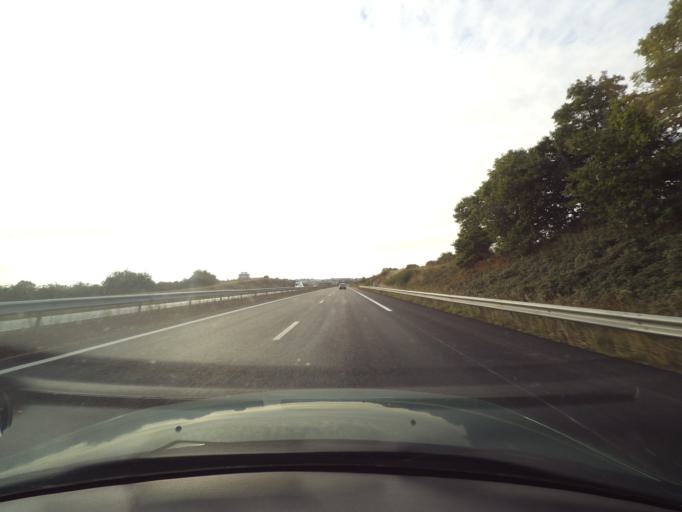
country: FR
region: Pays de la Loire
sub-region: Departement de Maine-et-Loire
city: La Seguiniere
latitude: 47.0783
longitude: -0.9577
